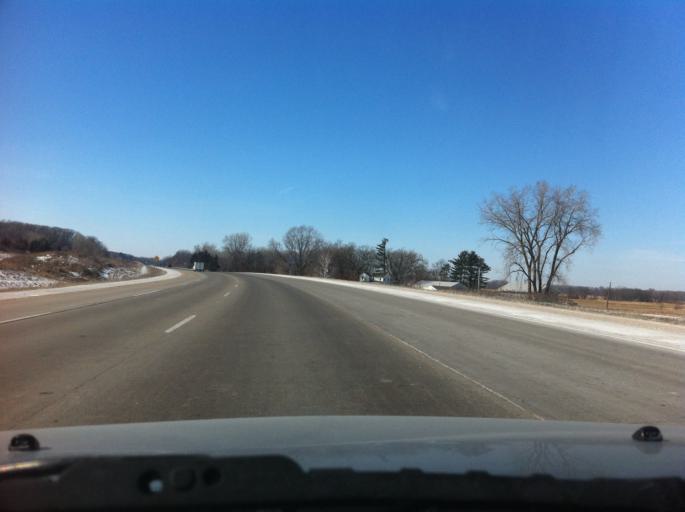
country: US
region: Wisconsin
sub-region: Columbia County
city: Portage
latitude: 43.4679
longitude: -89.4952
